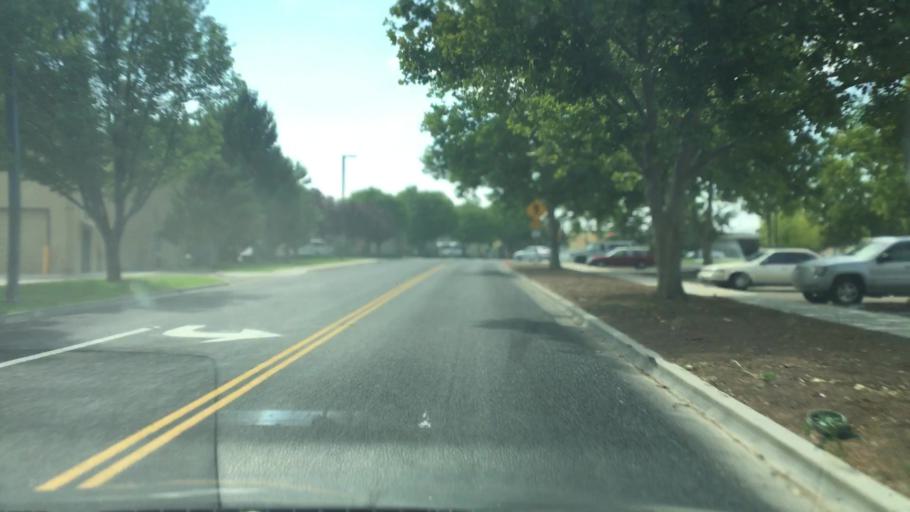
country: US
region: Idaho
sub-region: Ada County
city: Garden City
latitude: 43.6067
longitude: -116.2710
